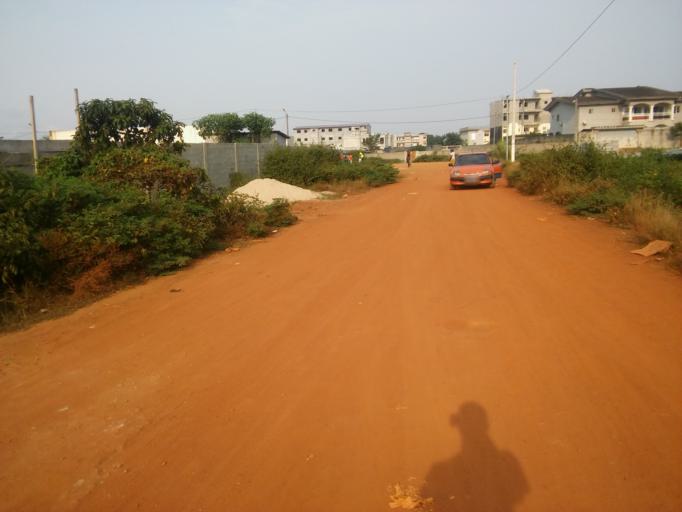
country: CI
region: Sud-Comoe
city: Grand-Bassam
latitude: 5.2121
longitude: -3.7614
